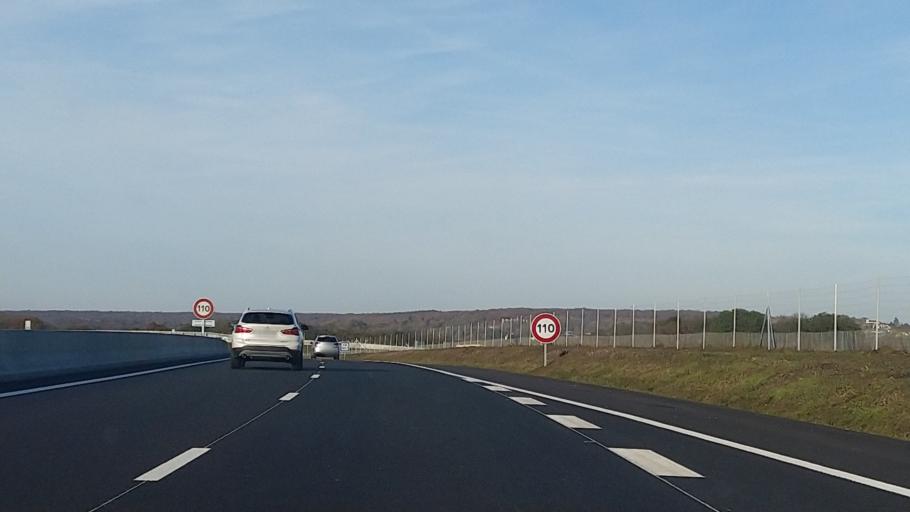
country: FR
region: Ile-de-France
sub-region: Departement du Val-d'Oise
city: Montsoult
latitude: 49.0744
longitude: 2.3329
